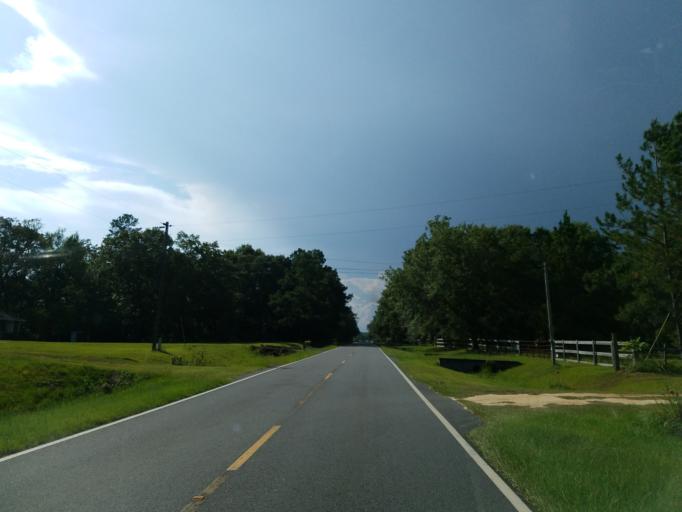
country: US
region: Georgia
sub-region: Lowndes County
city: Hahira
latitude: 31.0245
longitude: -83.4378
